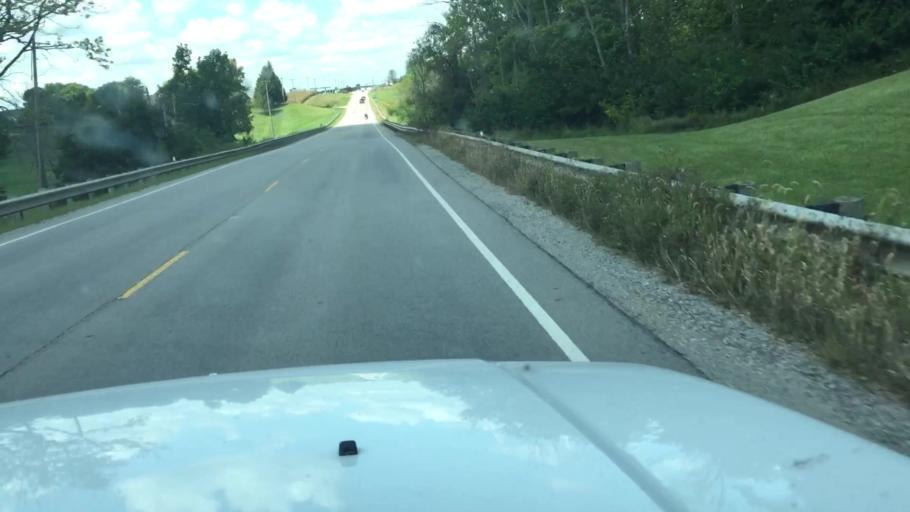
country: US
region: Ohio
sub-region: Madison County
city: Mount Sterling
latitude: 39.7521
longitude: -83.2932
